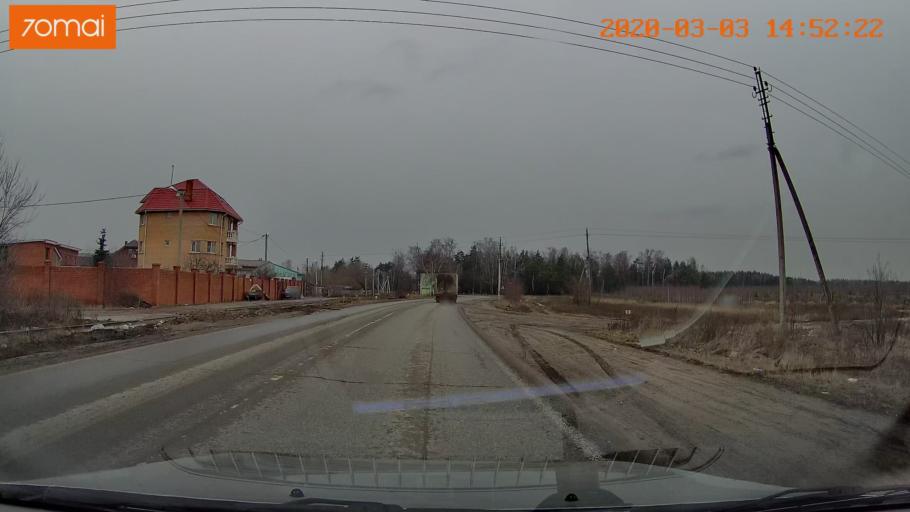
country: RU
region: Moskovskaya
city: Korenevo
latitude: 55.6702
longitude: 38.0159
